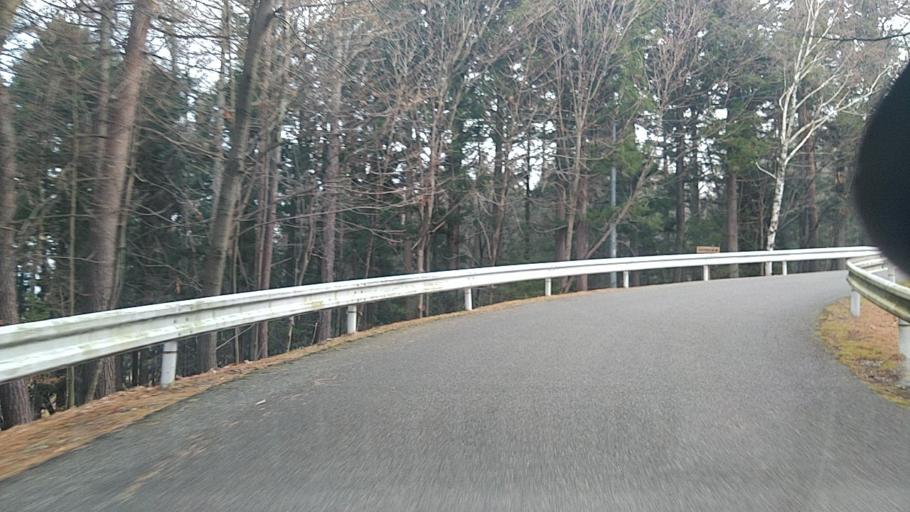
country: JP
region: Nagano
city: Shiojiri
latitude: 36.1442
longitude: 137.9925
